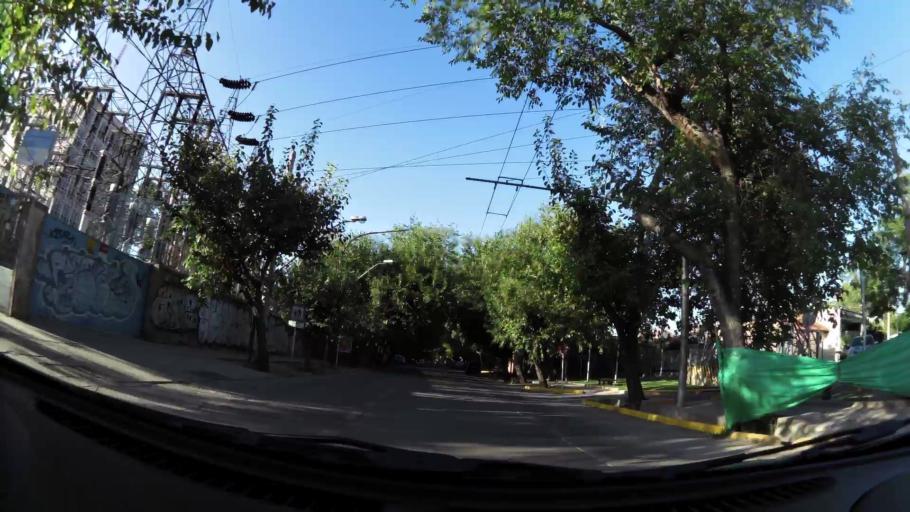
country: AR
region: Mendoza
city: Mendoza
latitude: -32.8996
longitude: -68.8431
